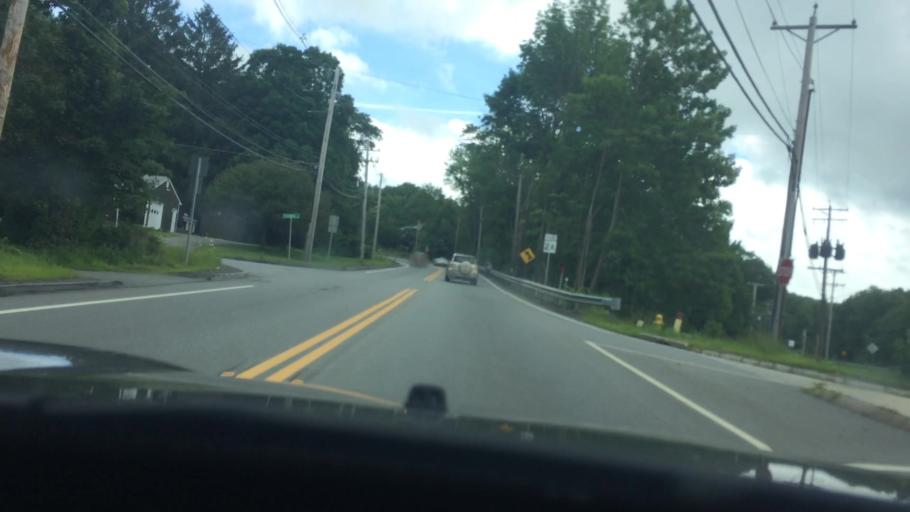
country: US
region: Massachusetts
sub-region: Worcester County
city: Athol
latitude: 42.5827
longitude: -72.2029
